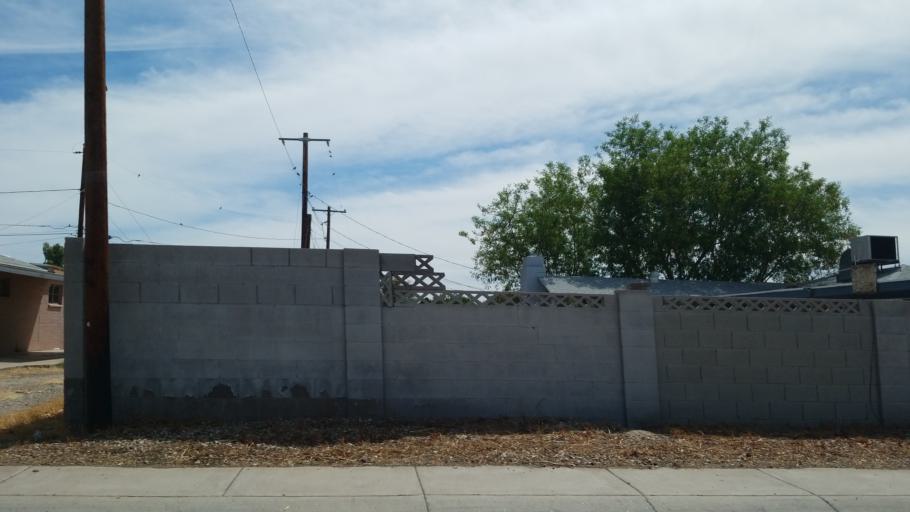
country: US
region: Arizona
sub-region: Maricopa County
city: Glendale
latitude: 33.5570
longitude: -112.1256
